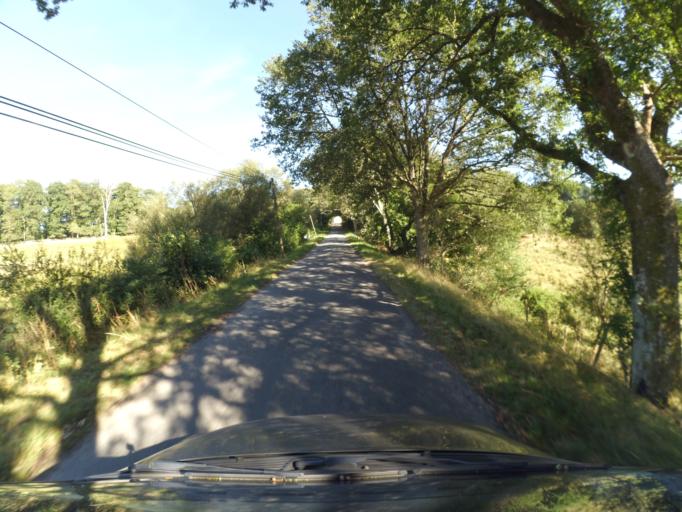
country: FR
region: Limousin
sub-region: Departement de la Correze
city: Bugeat
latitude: 45.6824
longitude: 1.9437
